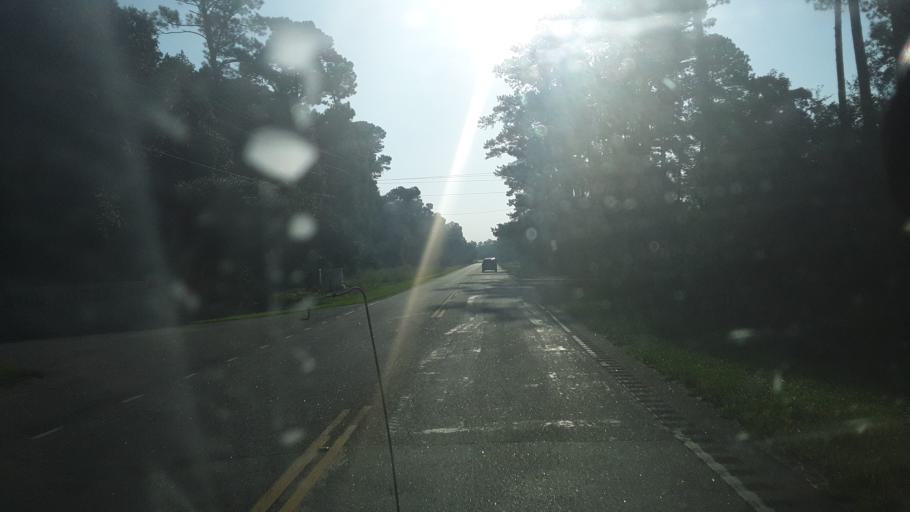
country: US
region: South Carolina
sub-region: Horry County
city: Red Hill
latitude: 33.8219
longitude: -78.9111
